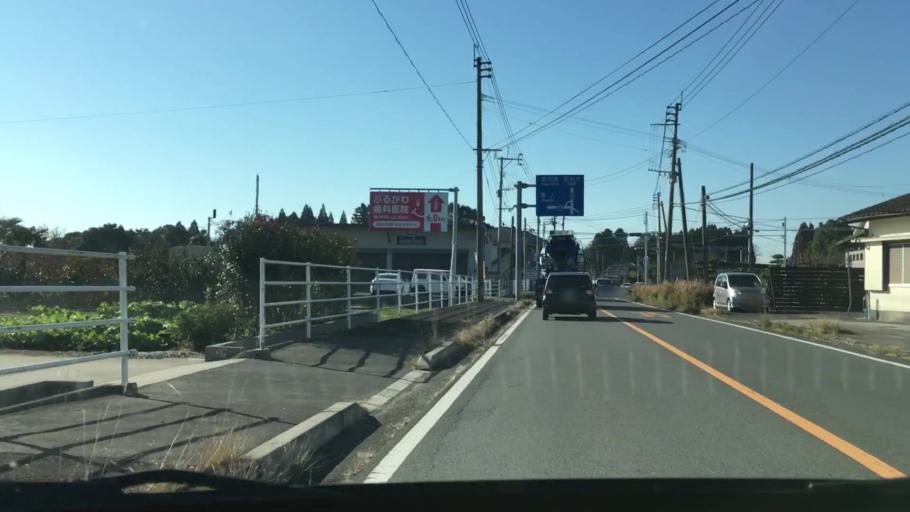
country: JP
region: Kagoshima
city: Kajiki
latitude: 31.7790
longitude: 130.7032
